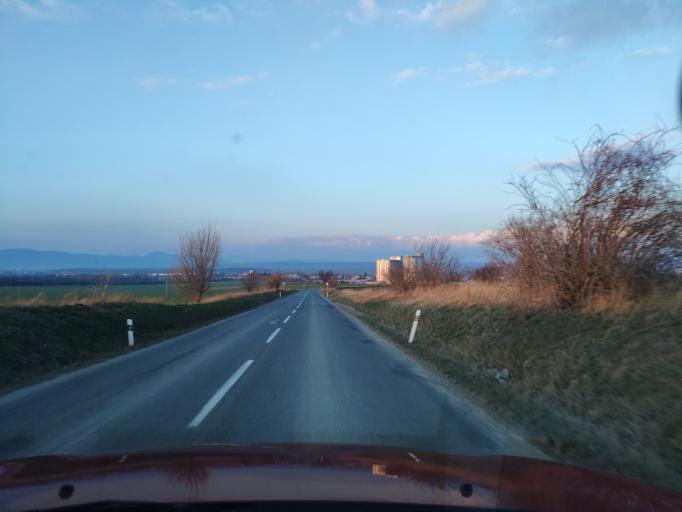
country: SK
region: Nitriansky
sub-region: Okres Nitra
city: Nitra
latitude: 48.2314
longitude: 18.1054
